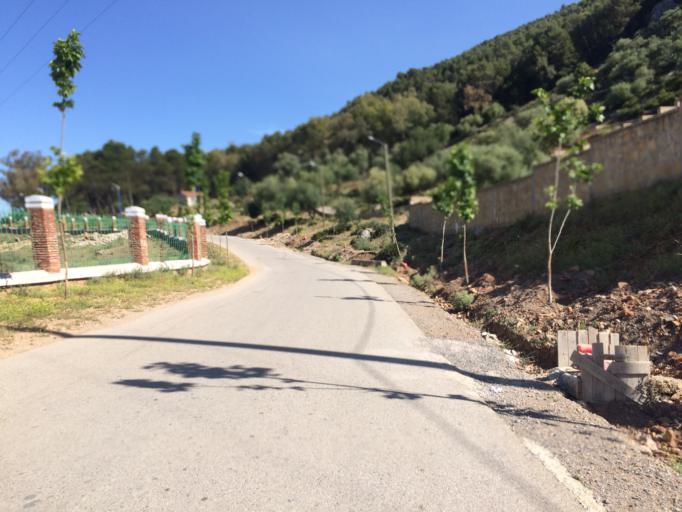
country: MA
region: Tanger-Tetouan
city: Chefchaouene
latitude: 35.1728
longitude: -5.2617
